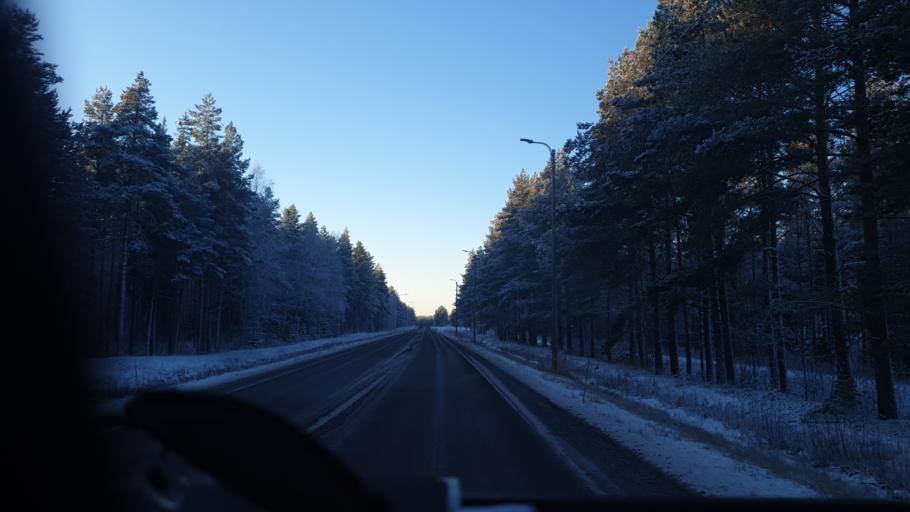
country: FI
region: Northern Ostrobothnia
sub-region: Ylivieska
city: Kalajoki
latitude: 64.2426
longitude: 23.8518
